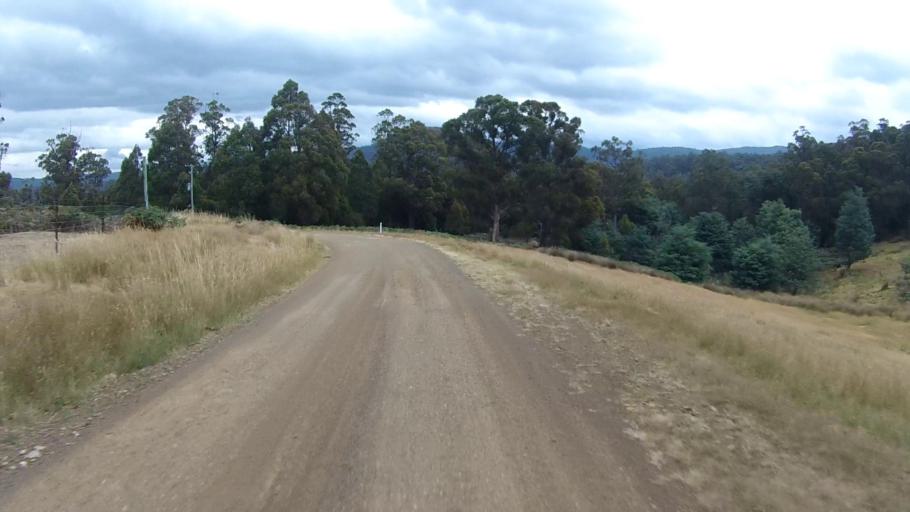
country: AU
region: Tasmania
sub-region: Huon Valley
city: Huonville
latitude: -42.9579
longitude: 147.0503
